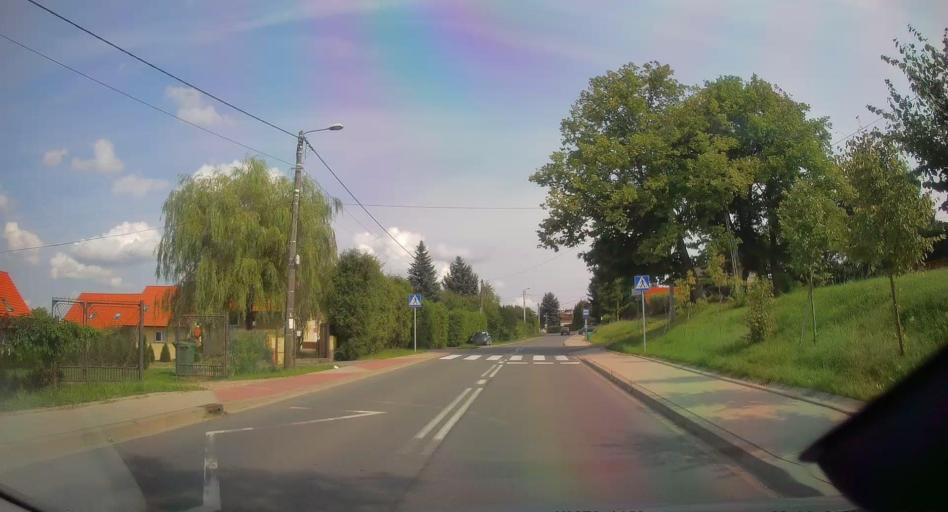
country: PL
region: Lesser Poland Voivodeship
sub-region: Powiat wielicki
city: Wieliczka
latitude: 49.9741
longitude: 20.0565
